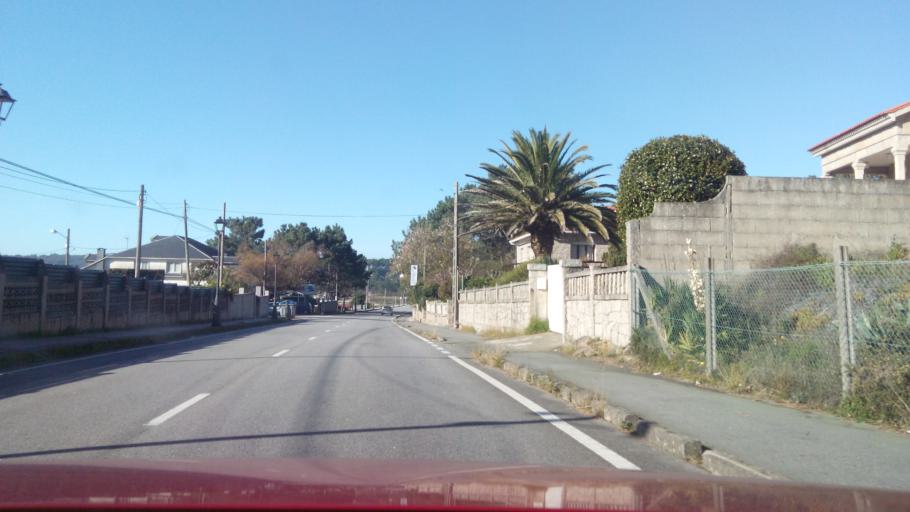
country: ES
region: Galicia
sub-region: Provincia de Pontevedra
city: O Grove
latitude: 42.4597
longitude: -8.8926
